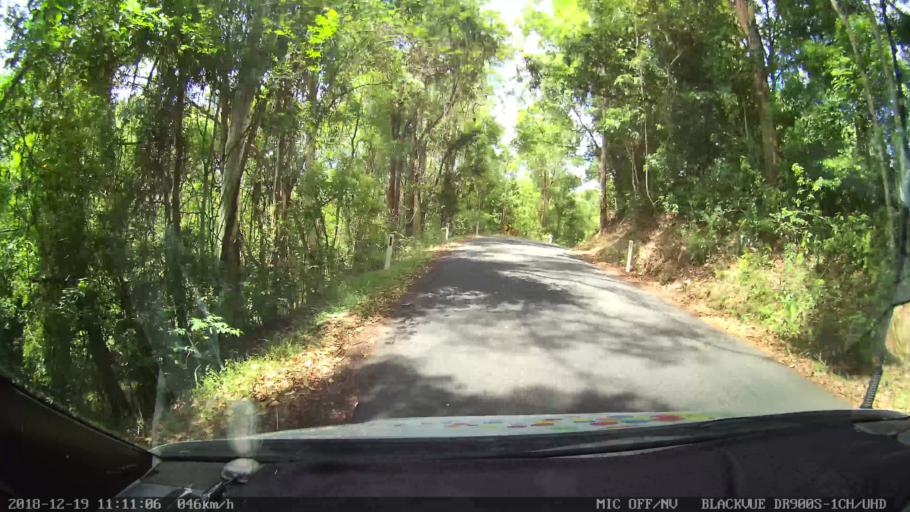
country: AU
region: New South Wales
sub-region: Lismore Municipality
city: Nimbin
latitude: -28.6420
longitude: 153.2587
